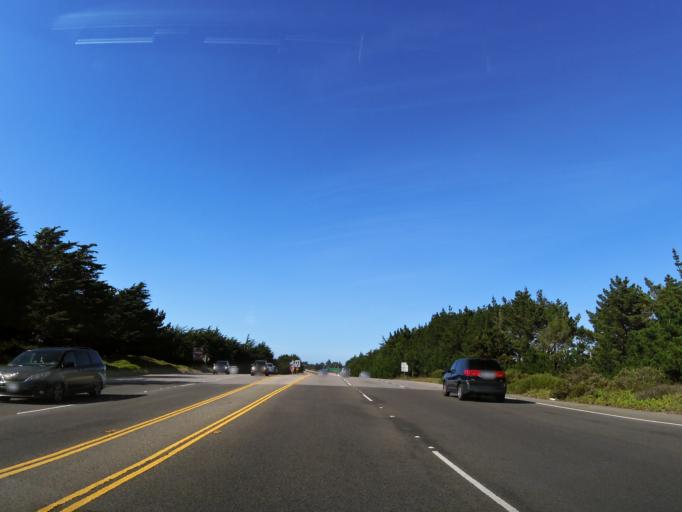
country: US
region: California
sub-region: San Mateo County
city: Colma
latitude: 37.6623
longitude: -122.4771
